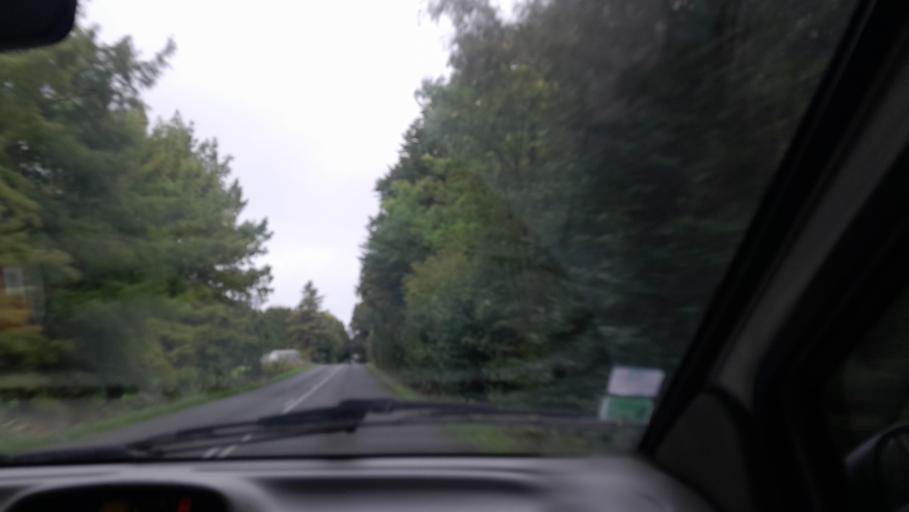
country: FR
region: Pays de la Loire
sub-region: Departement de Maine-et-Loire
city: Pouance
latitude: 47.7082
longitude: -1.1790
